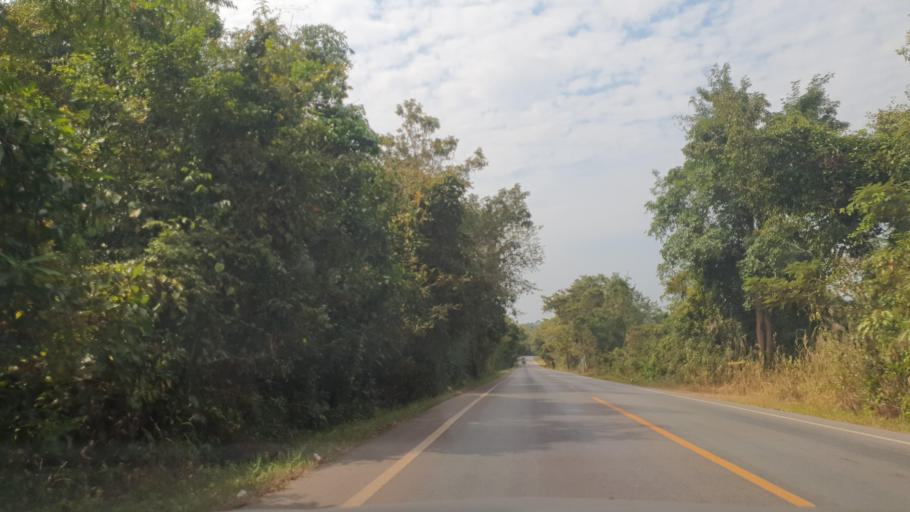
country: TH
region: Changwat Bueng Kan
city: Bung Khla
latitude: 18.2883
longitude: 103.9025
